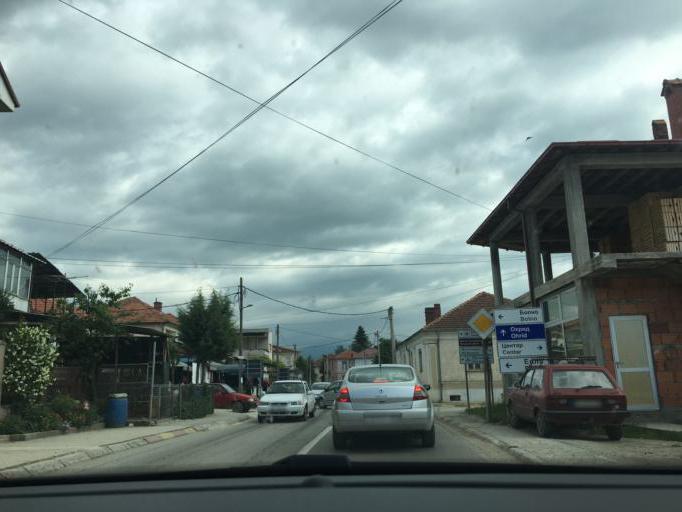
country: MK
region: Resen
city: Resen
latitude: 41.0879
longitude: 21.0092
